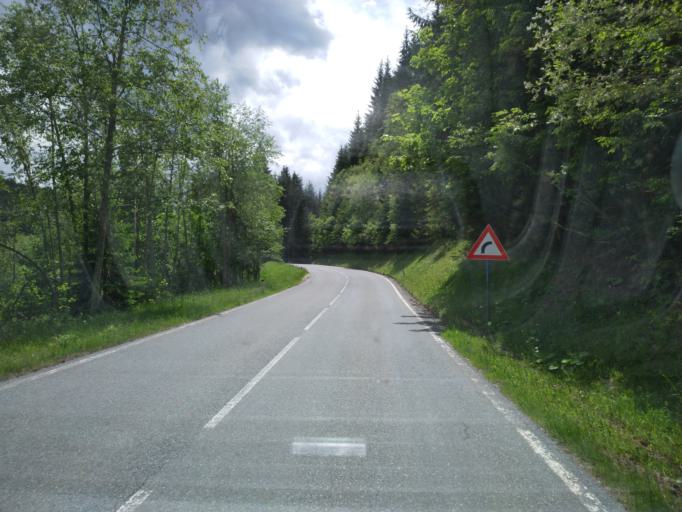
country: AT
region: Salzburg
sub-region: Politischer Bezirk Sankt Johann im Pongau
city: Filzmoos
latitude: 47.4420
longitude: 13.5774
